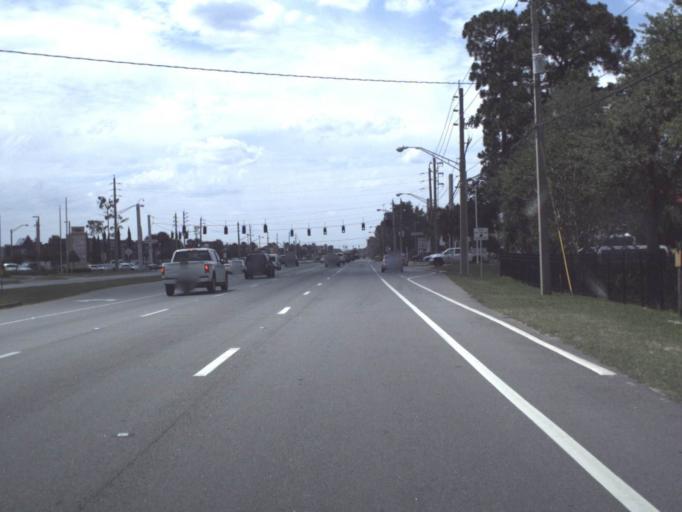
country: US
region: Florida
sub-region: Saint Johns County
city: Fruit Cove
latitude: 30.2193
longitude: -81.5848
